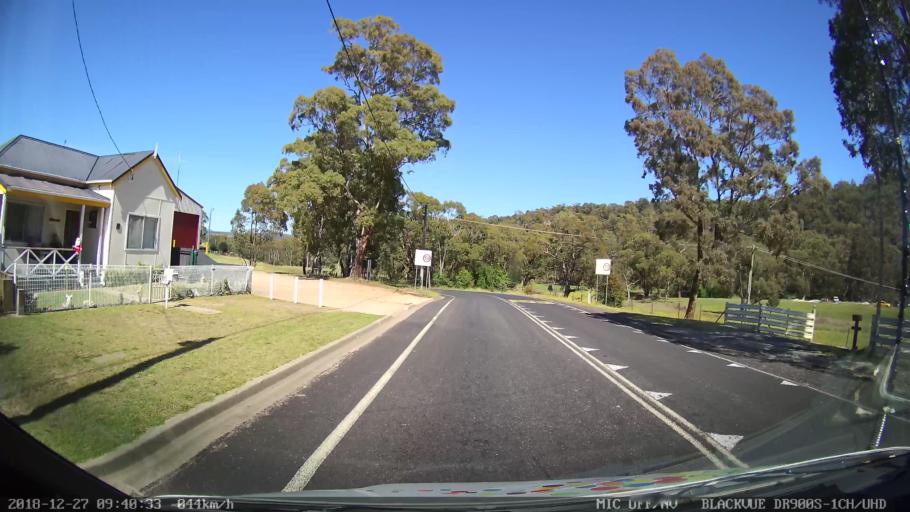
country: AU
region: New South Wales
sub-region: Lithgow
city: Portland
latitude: -33.2994
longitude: 150.0313
